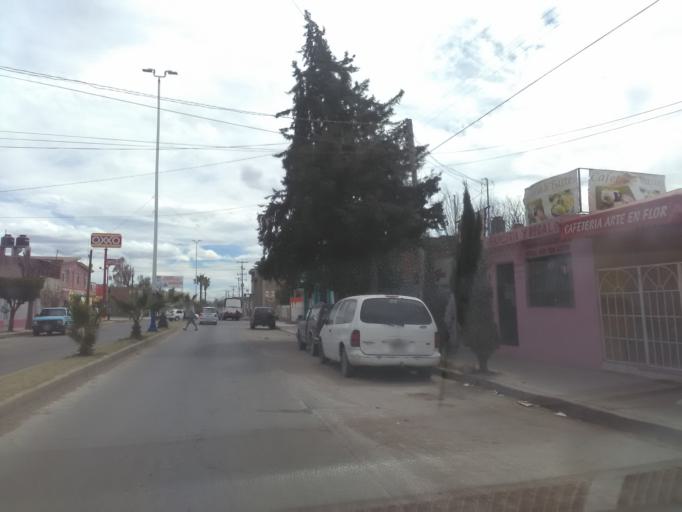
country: MX
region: Durango
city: Victoria de Durango
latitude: 24.0496
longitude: -104.6867
